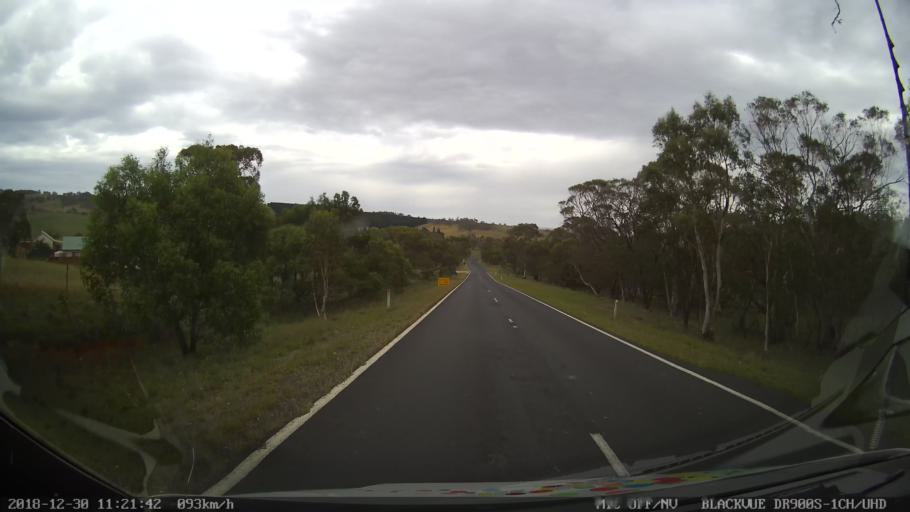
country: AU
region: New South Wales
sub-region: Snowy River
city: Jindabyne
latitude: -36.5079
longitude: 148.6748
